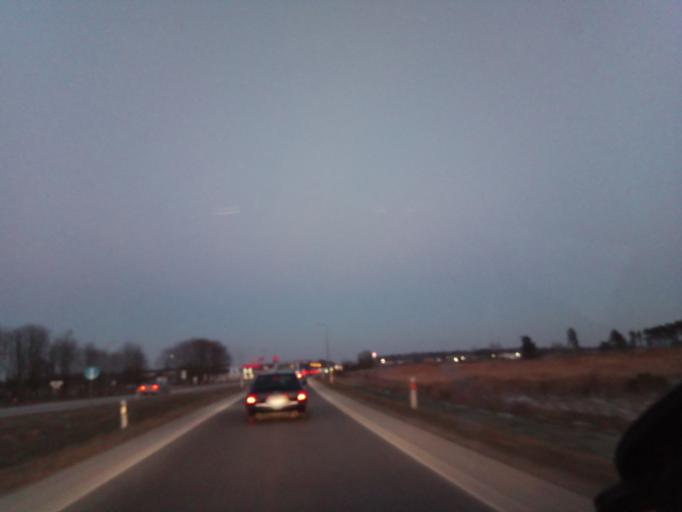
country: LT
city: Lentvaris
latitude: 54.6216
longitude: 25.1023
